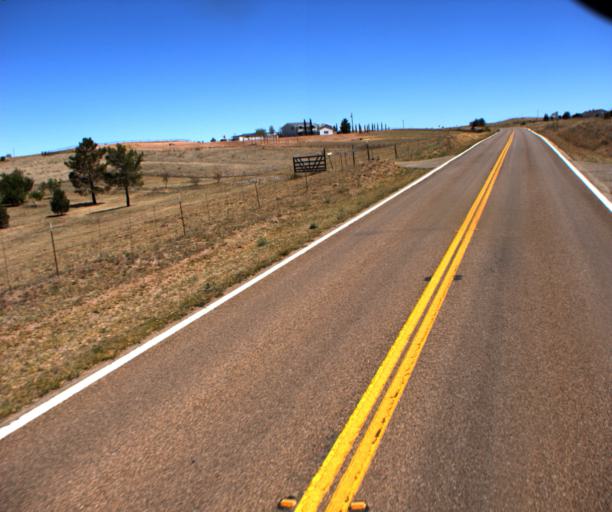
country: US
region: Arizona
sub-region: Cochise County
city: Huachuca City
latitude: 31.6710
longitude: -110.6091
